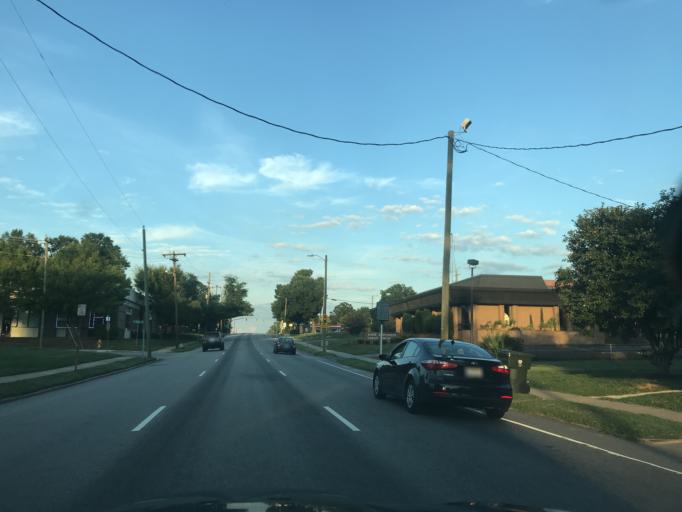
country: US
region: North Carolina
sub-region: Wake County
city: Raleigh
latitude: 35.7800
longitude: -78.6247
